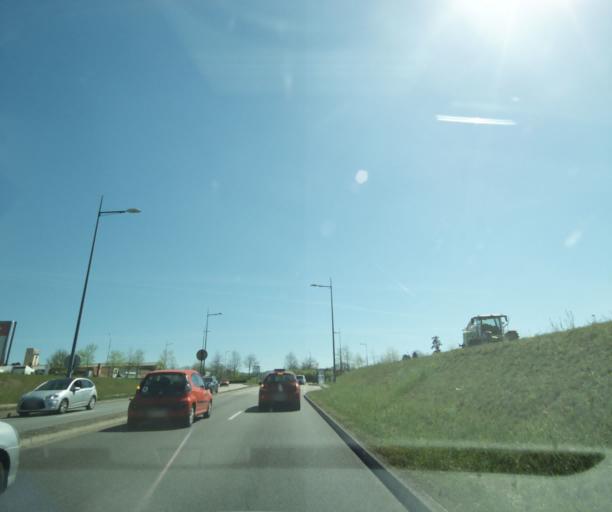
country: FR
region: Limousin
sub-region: Departement de la Haute-Vienne
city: Limoges
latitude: 45.8117
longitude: 1.2562
